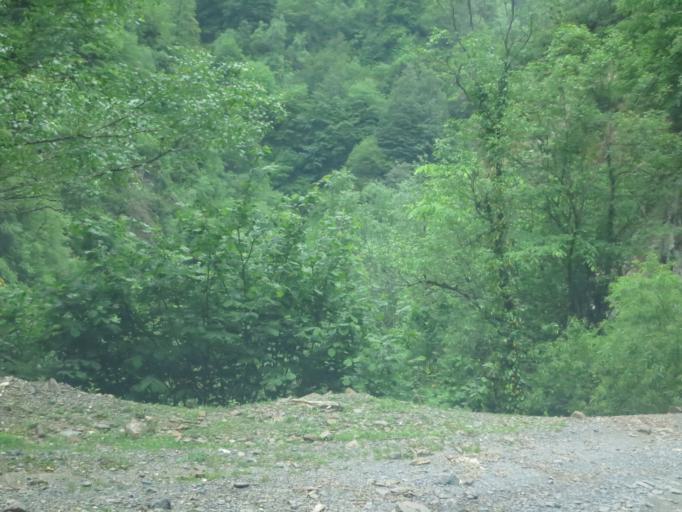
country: GE
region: Kakheti
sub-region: Telavi
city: Telavi
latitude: 42.2345
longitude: 45.4901
